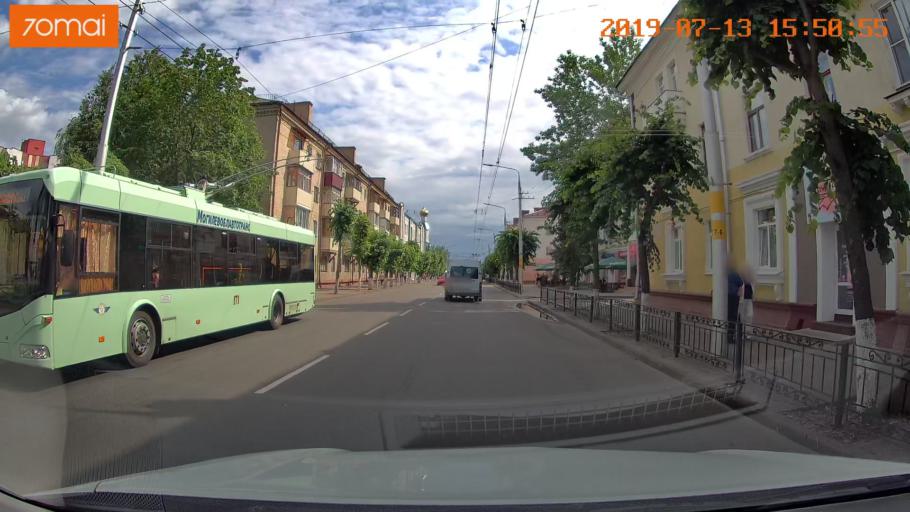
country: BY
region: Mogilev
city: Babruysk
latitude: 53.1412
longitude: 29.2244
